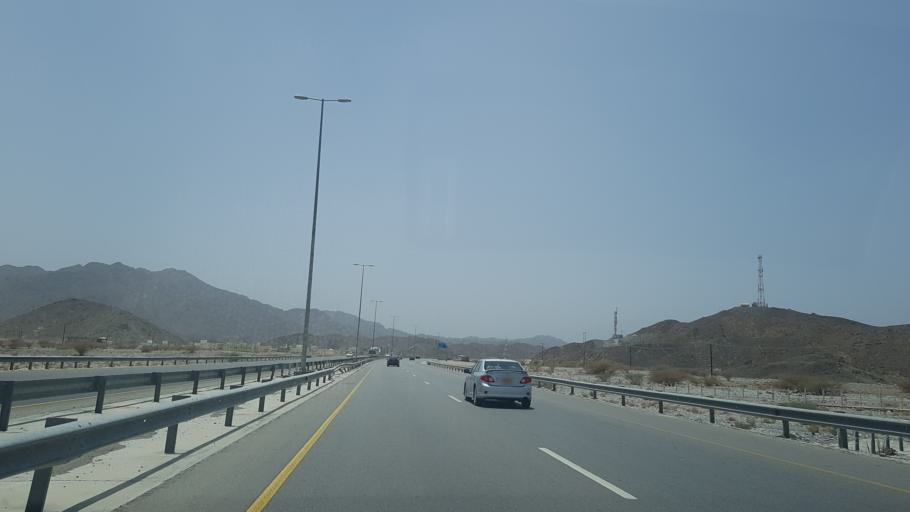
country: OM
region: Muhafazat ad Dakhiliyah
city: Sufalat Sama'il
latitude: 23.3763
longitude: 58.0502
